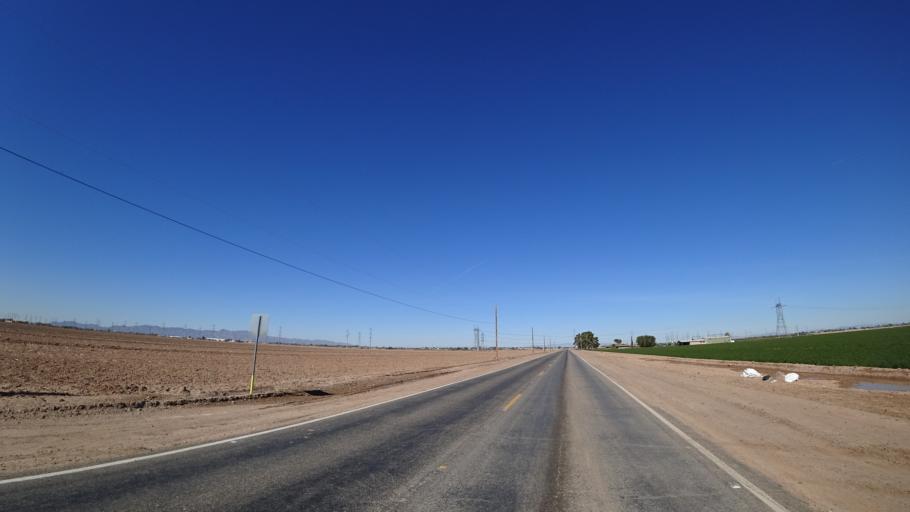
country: US
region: Arizona
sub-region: Maricopa County
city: Avondale
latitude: 33.3955
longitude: -112.3233
